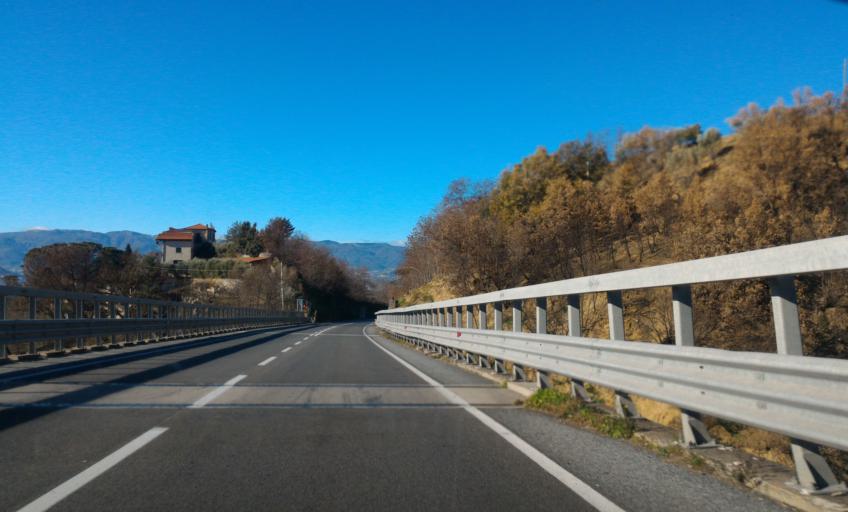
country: IT
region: Calabria
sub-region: Provincia di Cosenza
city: Zumpano
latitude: 39.2983
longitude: 16.2960
